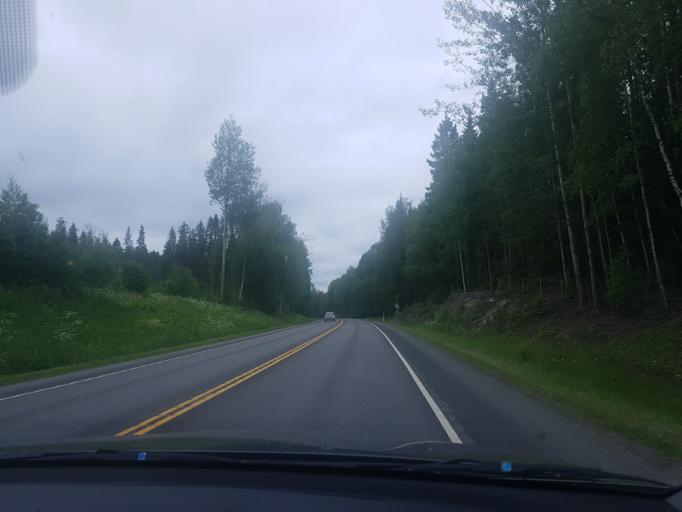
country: FI
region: Pirkanmaa
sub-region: Tampere
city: Paelkaene
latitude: 61.3970
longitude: 24.2093
